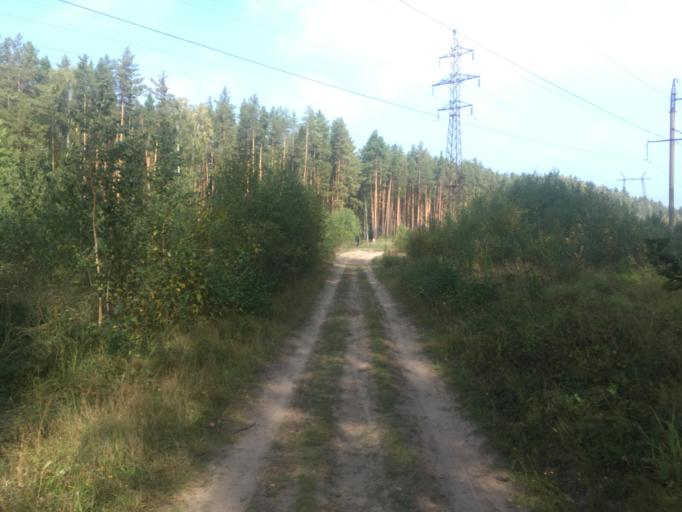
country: RU
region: Tatarstan
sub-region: Zelenodol'skiy Rayon
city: Zelenodolsk
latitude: 55.8633
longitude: 48.4867
